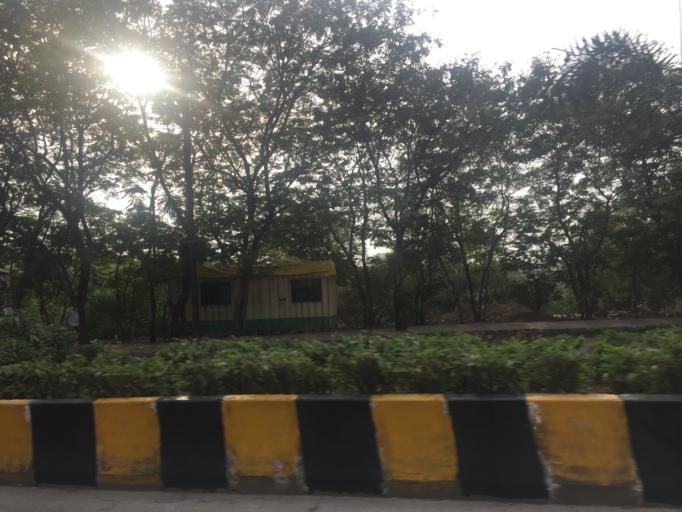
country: IN
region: Maharashtra
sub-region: Thane
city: Airoli
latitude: 19.1526
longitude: 72.9930
